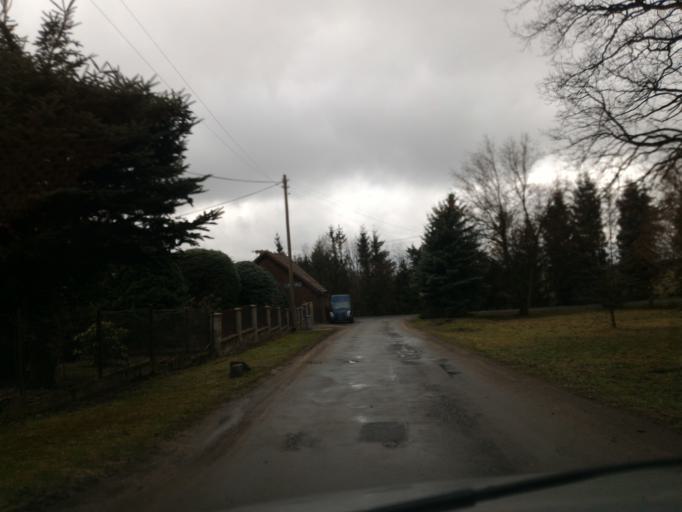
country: CZ
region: Liberecky
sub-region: Okres Liberec
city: Frydlant
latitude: 50.9308
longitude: 15.0713
